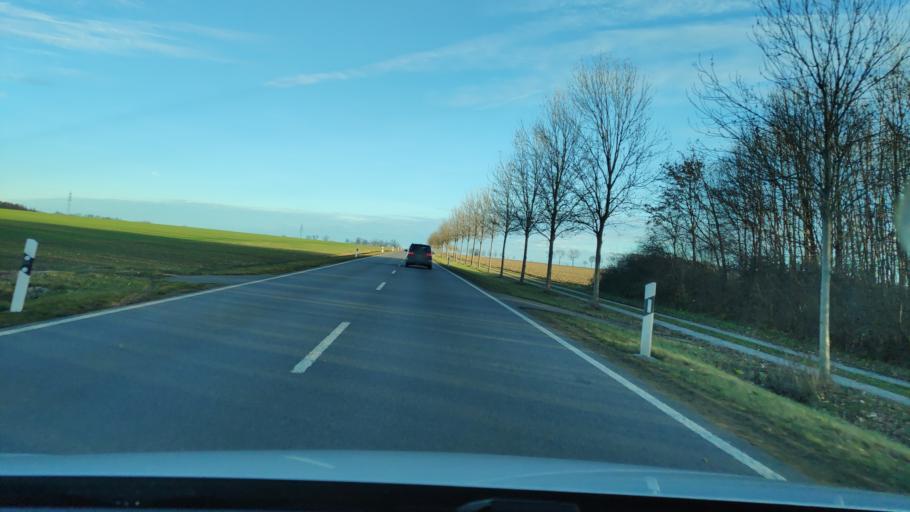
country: DE
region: Saxony
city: Zwickau
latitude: 50.7644
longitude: 12.5197
